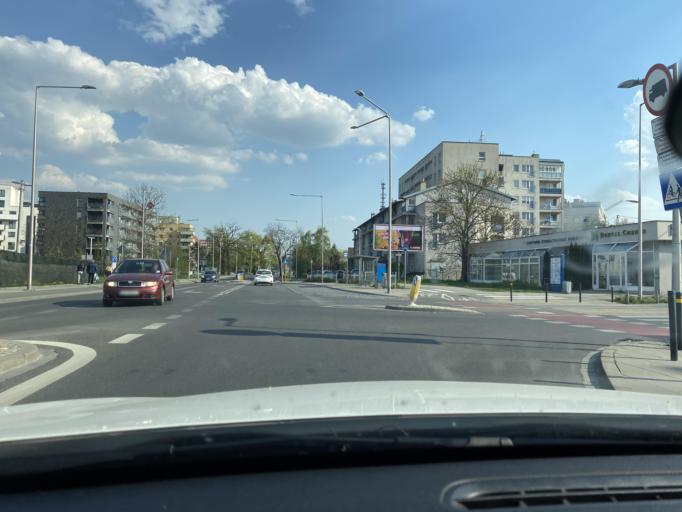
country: PL
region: Lower Silesian Voivodeship
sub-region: Powiat wroclawski
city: Wroclaw
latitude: 51.1418
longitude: 17.0261
